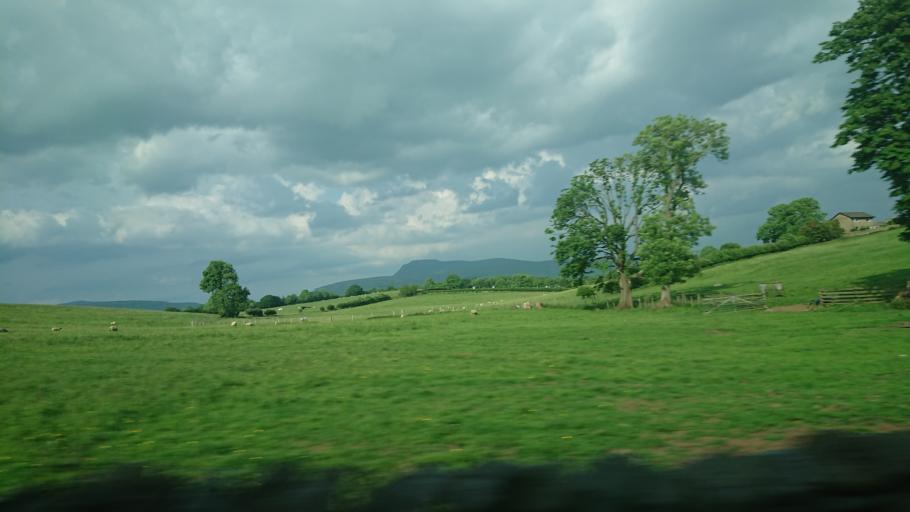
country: GB
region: England
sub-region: North Yorkshire
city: High Bentham
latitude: 54.1292
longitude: -2.5101
